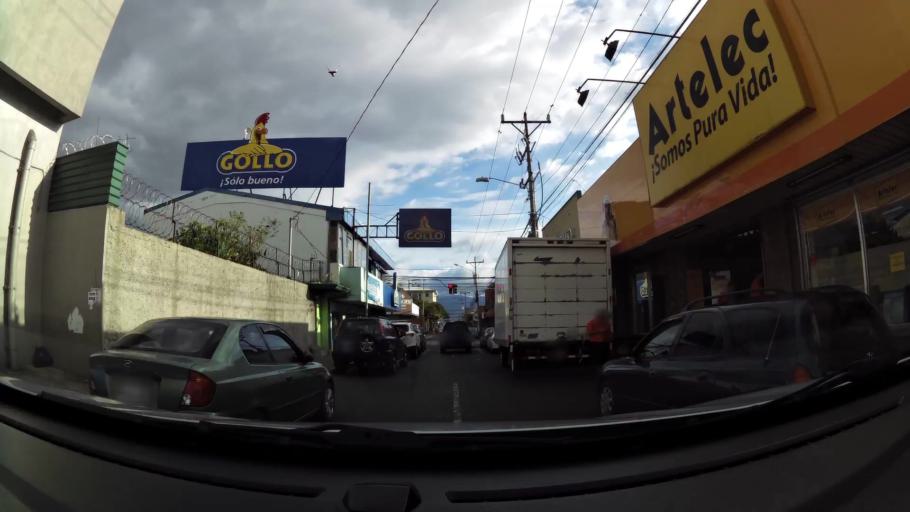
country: CR
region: Alajuela
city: Alajuela
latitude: 10.0153
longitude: -84.2149
